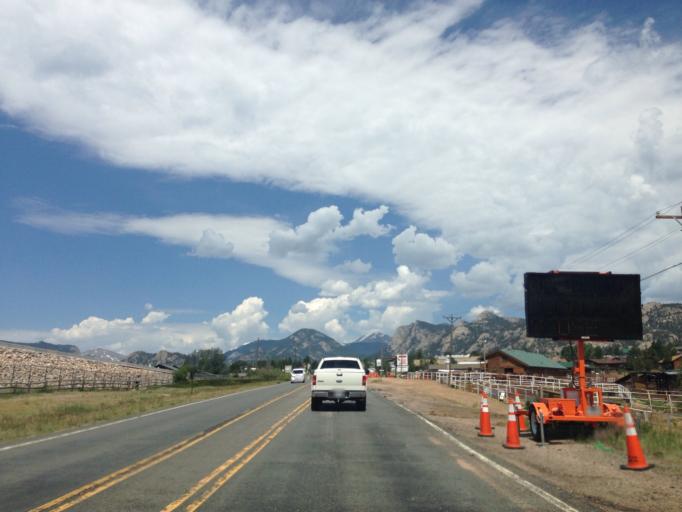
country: US
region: Colorado
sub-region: Larimer County
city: Estes Park
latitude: 40.3785
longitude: -105.4886
